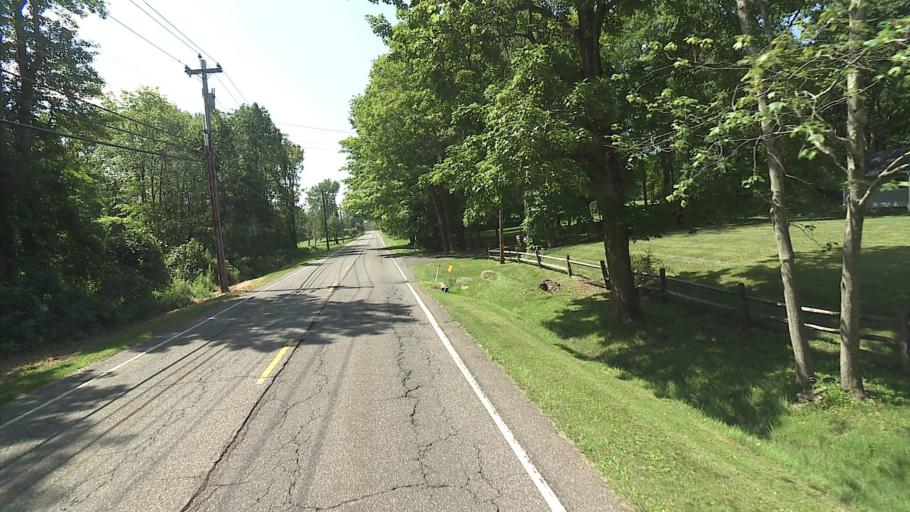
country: US
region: Connecticut
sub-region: Litchfield County
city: New Preston
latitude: 41.7165
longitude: -73.3441
